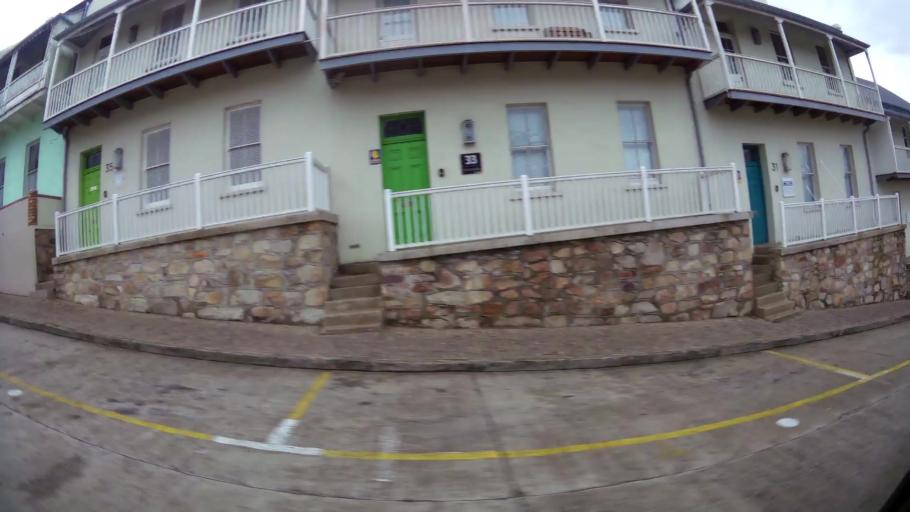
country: ZA
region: Eastern Cape
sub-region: Nelson Mandela Bay Metropolitan Municipality
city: Port Elizabeth
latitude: -33.9607
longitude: 25.6197
